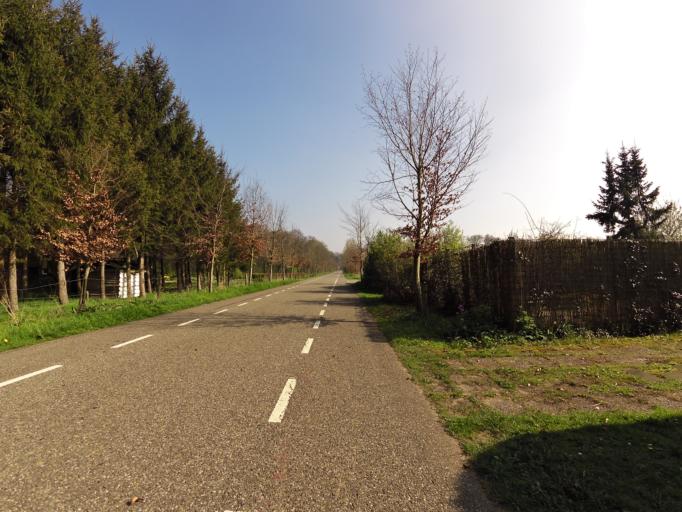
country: NL
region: Gelderland
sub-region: Gemeente Bronckhorst
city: Baak
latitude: 52.0755
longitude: 6.2335
